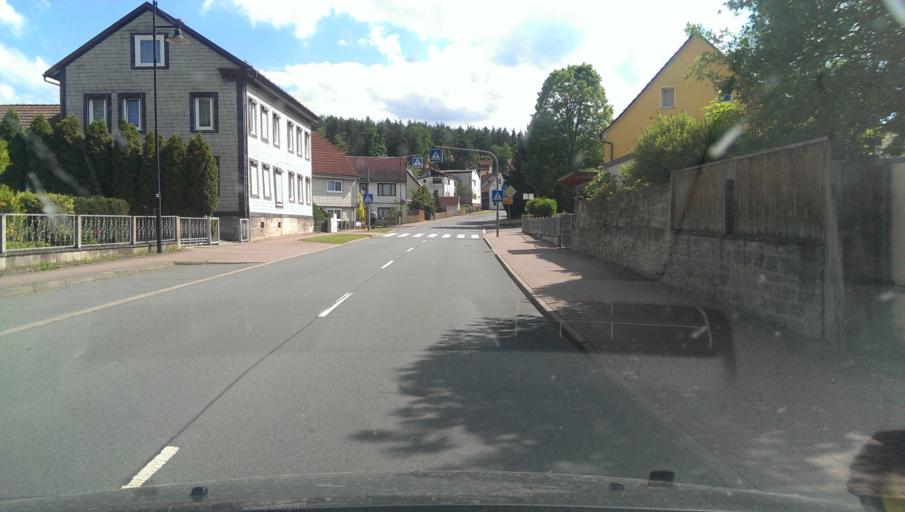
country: DE
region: Thuringia
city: Martinroda
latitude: 50.7244
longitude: 10.8880
